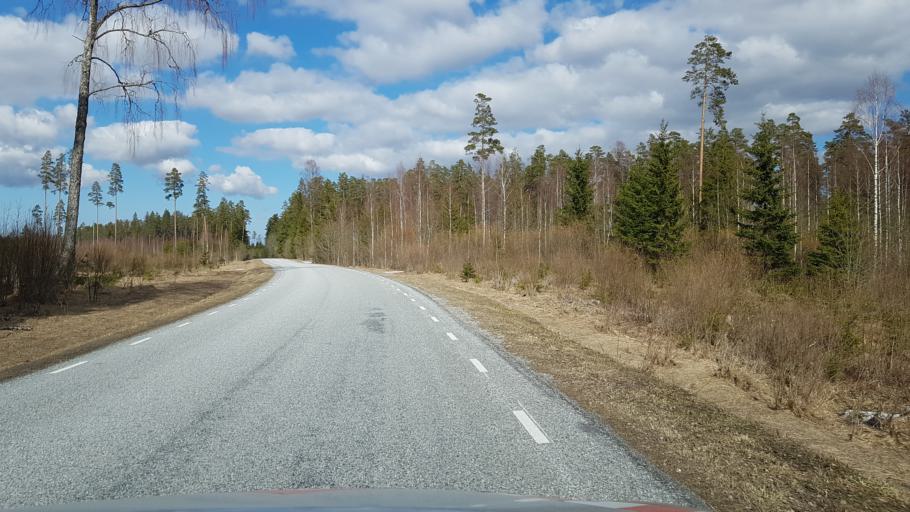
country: EE
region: Laeaene-Virumaa
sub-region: Tamsalu vald
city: Tamsalu
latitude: 59.2314
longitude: 26.1696
